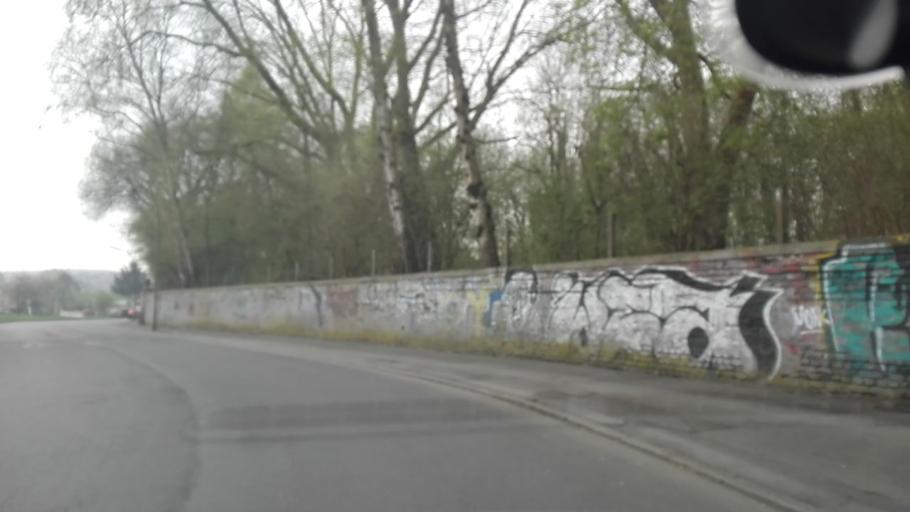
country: DE
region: North Rhine-Westphalia
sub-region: Regierungsbezirk Arnsberg
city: Dortmund
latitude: 51.4684
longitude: 7.4257
